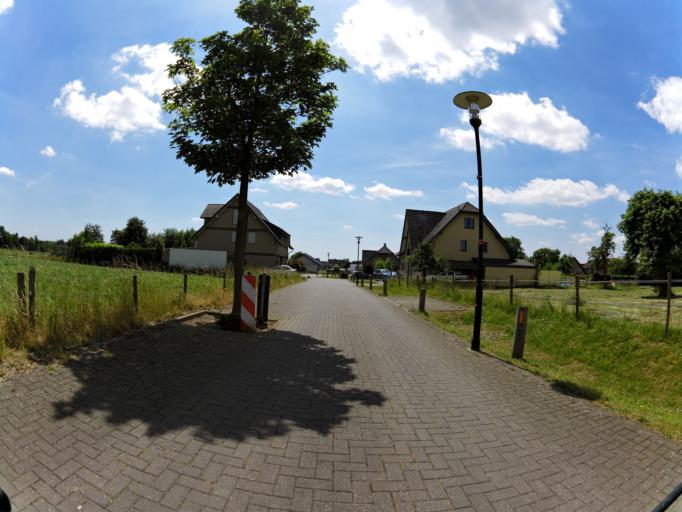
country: DE
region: North Rhine-Westphalia
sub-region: Regierungsbezirk Koln
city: Waldfeucht
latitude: 51.0292
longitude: 5.9920
